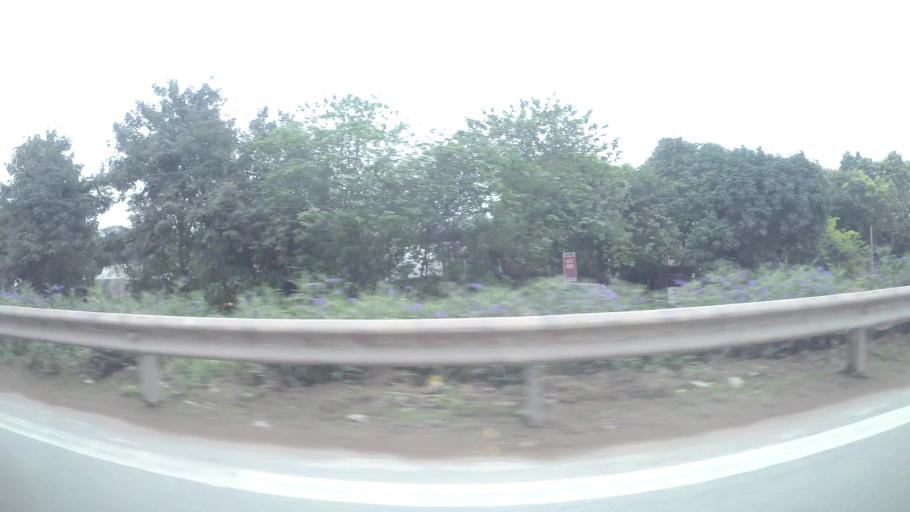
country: VN
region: Ha Noi
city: Trau Quy
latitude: 20.9872
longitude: 105.8947
